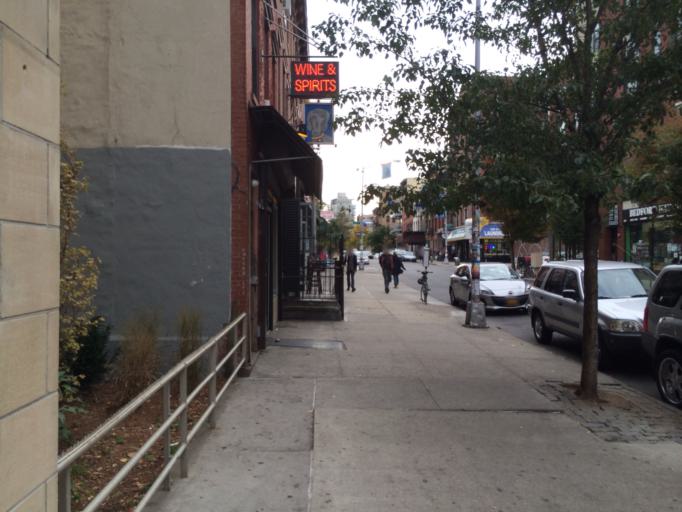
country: US
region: New York
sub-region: Queens County
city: Long Island City
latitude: 40.7138
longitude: -73.9618
